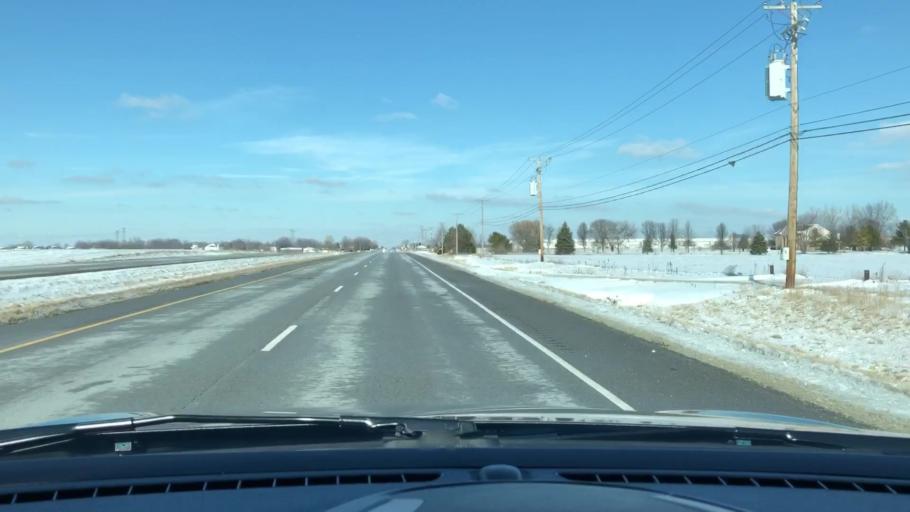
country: US
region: Illinois
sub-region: Will County
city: Elwood
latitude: 41.4379
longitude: -88.0786
